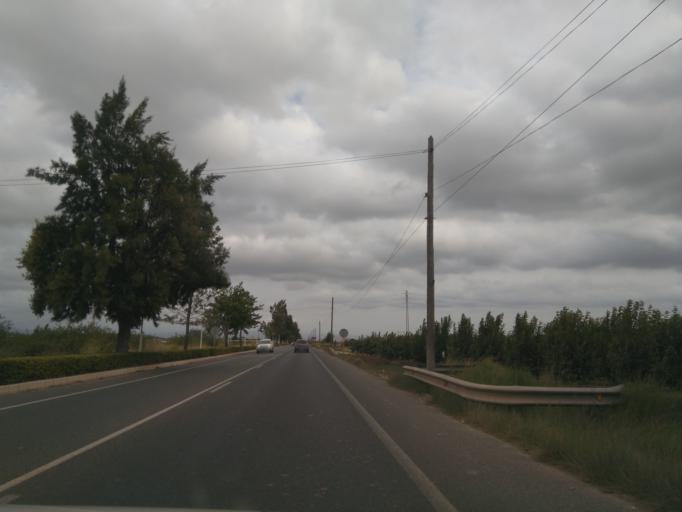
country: ES
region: Valencia
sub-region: Provincia de Valencia
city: Carlet
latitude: 39.2164
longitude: -0.5155
